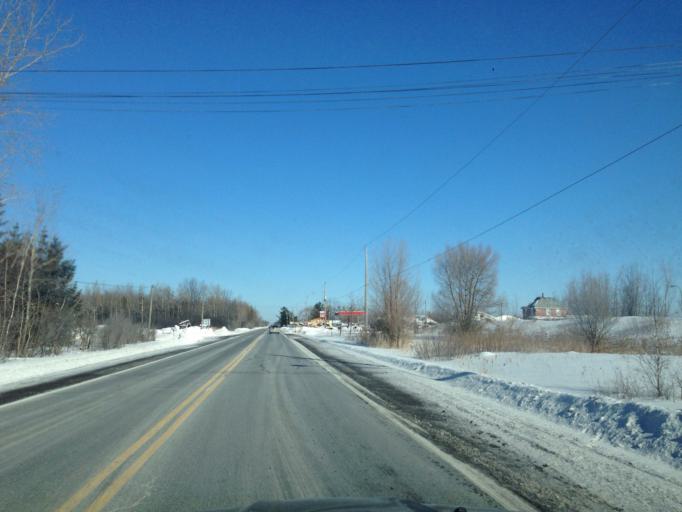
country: CA
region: Ontario
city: Clarence-Rockland
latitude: 45.3382
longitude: -75.4396
